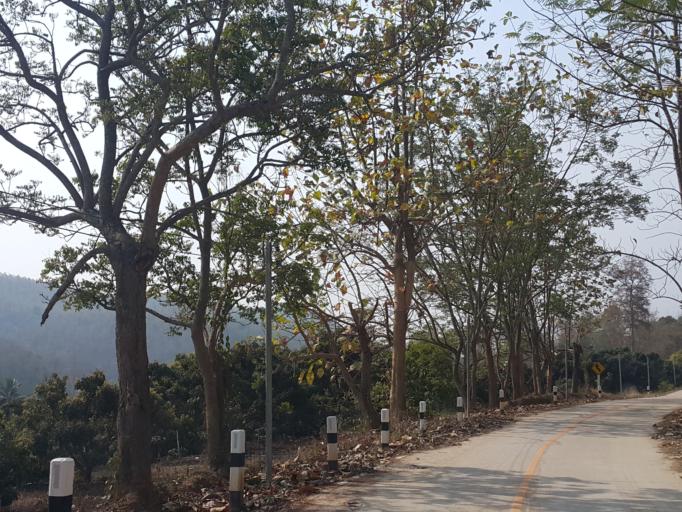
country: TH
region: Chiang Mai
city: Hang Dong
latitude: 18.7385
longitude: 98.8613
